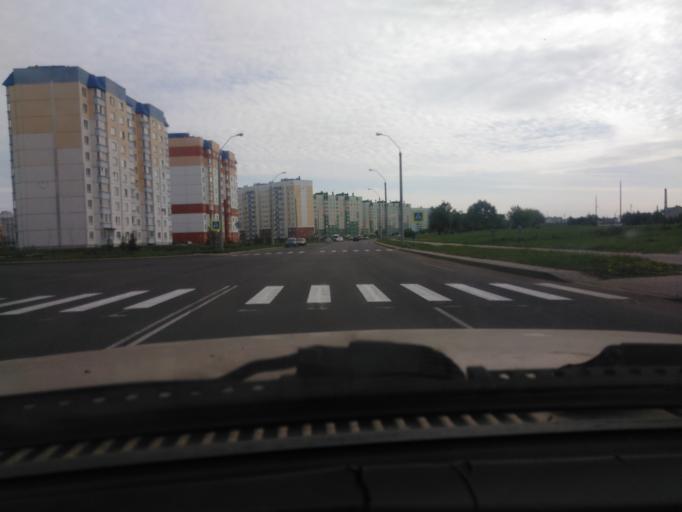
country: BY
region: Mogilev
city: Mahilyow
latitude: 53.9134
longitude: 30.2862
